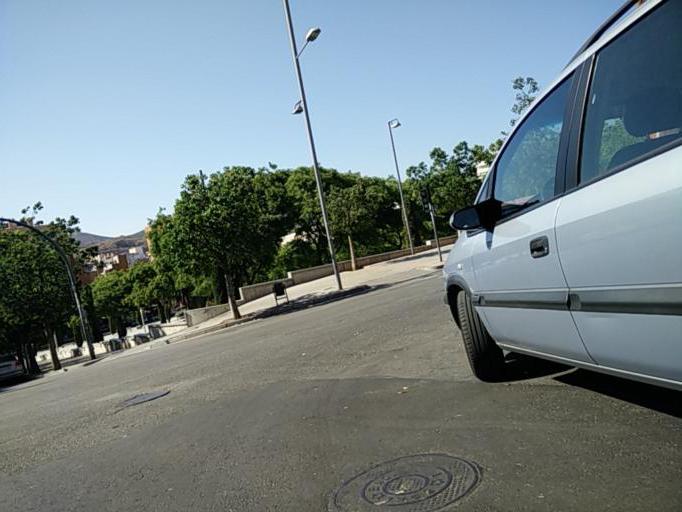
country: ES
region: Catalonia
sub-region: Provincia de Barcelona
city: Llefia
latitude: 41.4520
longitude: 2.2239
